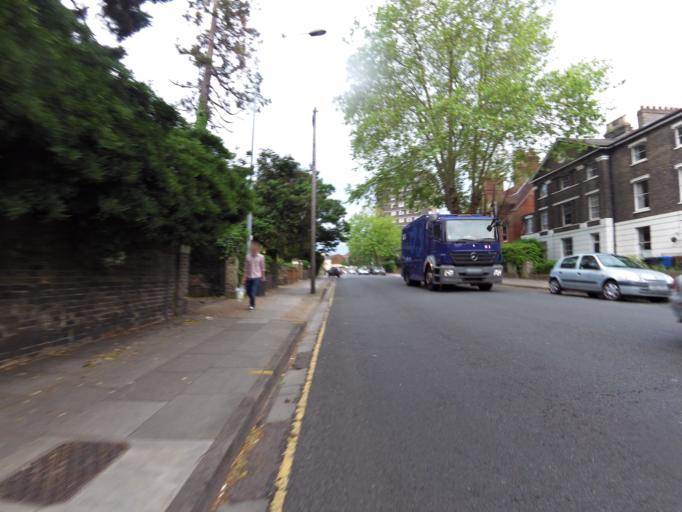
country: GB
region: England
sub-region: Suffolk
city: Ipswich
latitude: 52.0632
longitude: 1.1416
